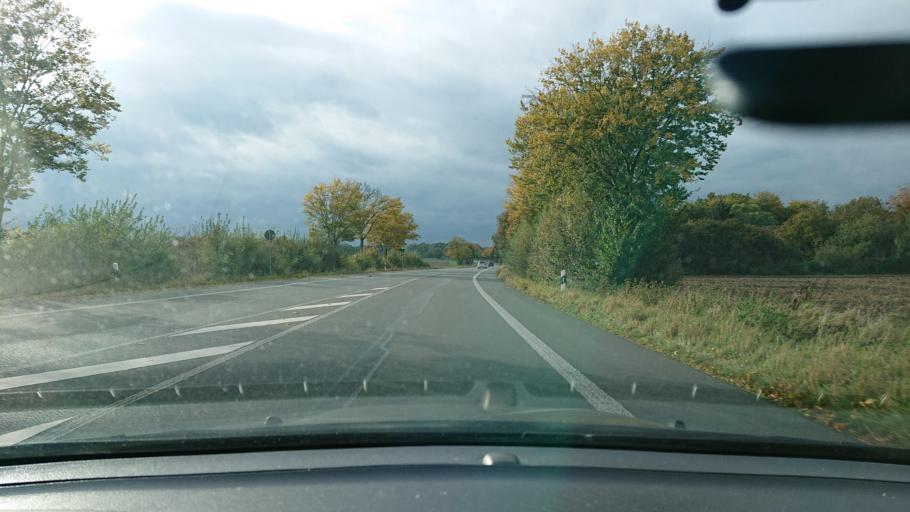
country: DE
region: North Rhine-Westphalia
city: Rietberg
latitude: 51.7461
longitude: 8.4469
